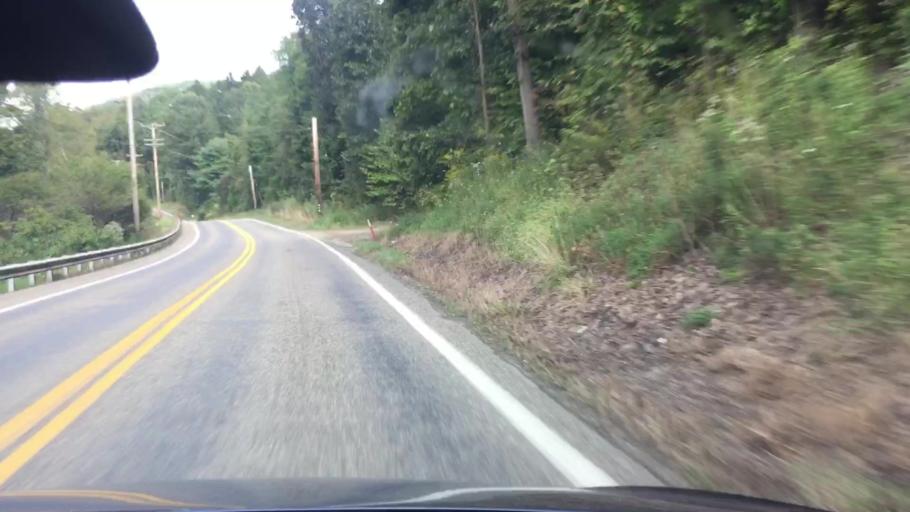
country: US
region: Pennsylvania
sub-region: Allegheny County
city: Cheswick
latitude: 40.5685
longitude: -79.8206
